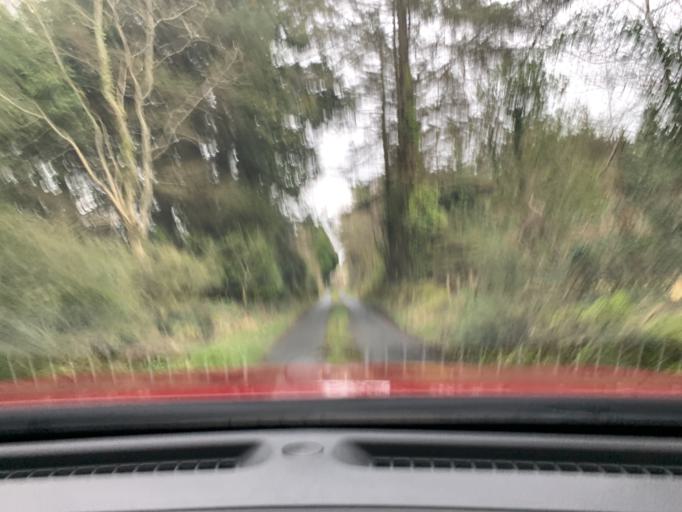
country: IE
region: Connaught
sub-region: Roscommon
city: Ballaghaderreen
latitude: 53.9648
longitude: -8.5061
